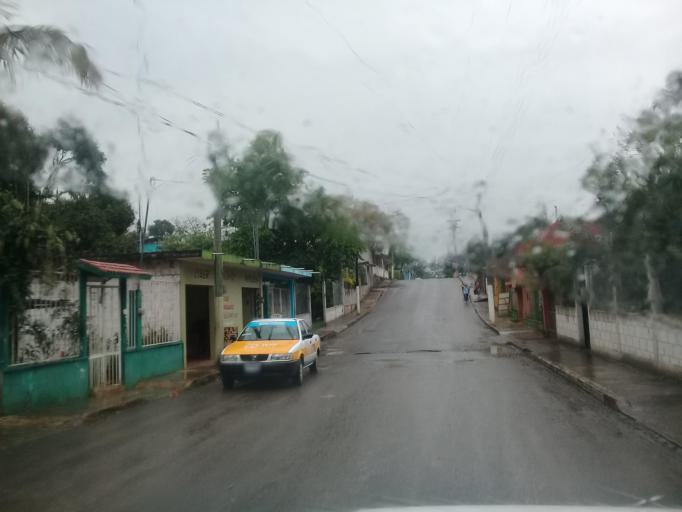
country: MX
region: Veracruz
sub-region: Cordoba
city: San Jose de Tapia
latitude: 18.8460
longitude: -96.9559
